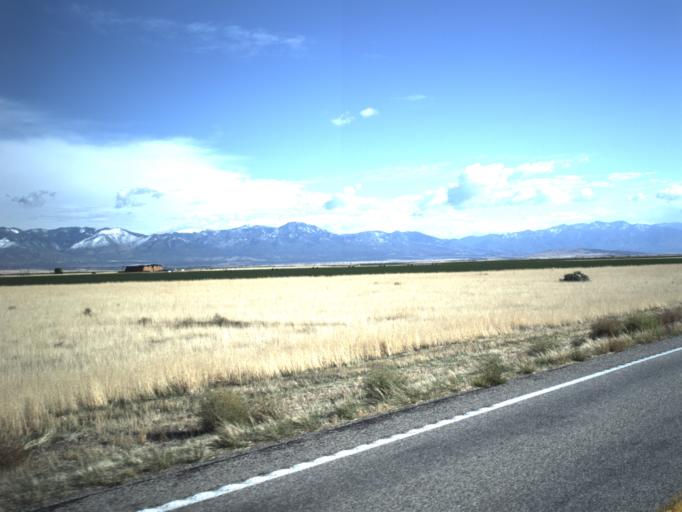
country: US
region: Utah
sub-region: Millard County
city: Delta
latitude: 39.1990
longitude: -112.4100
